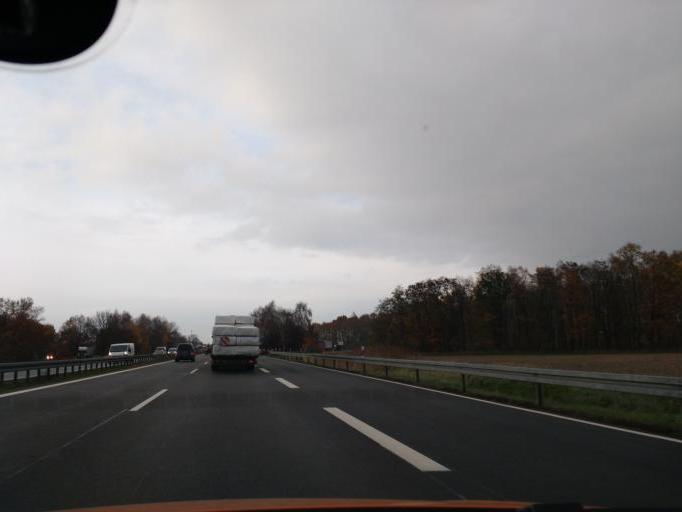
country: DE
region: Brandenburg
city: Dabergotz
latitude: 52.8858
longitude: 12.7541
